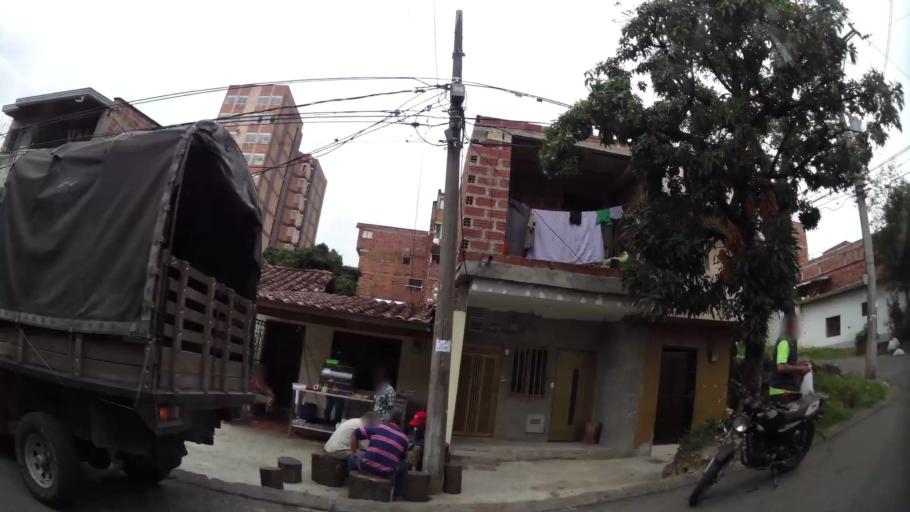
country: CO
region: Antioquia
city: Medellin
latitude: 6.2731
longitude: -75.5604
